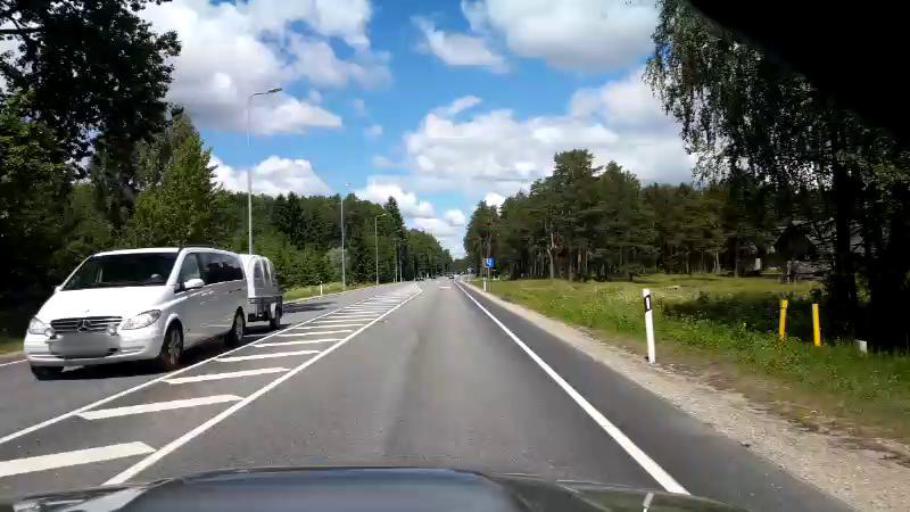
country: EE
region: Paernumaa
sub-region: Paikuse vald
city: Paikuse
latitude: 58.3236
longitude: 24.5978
